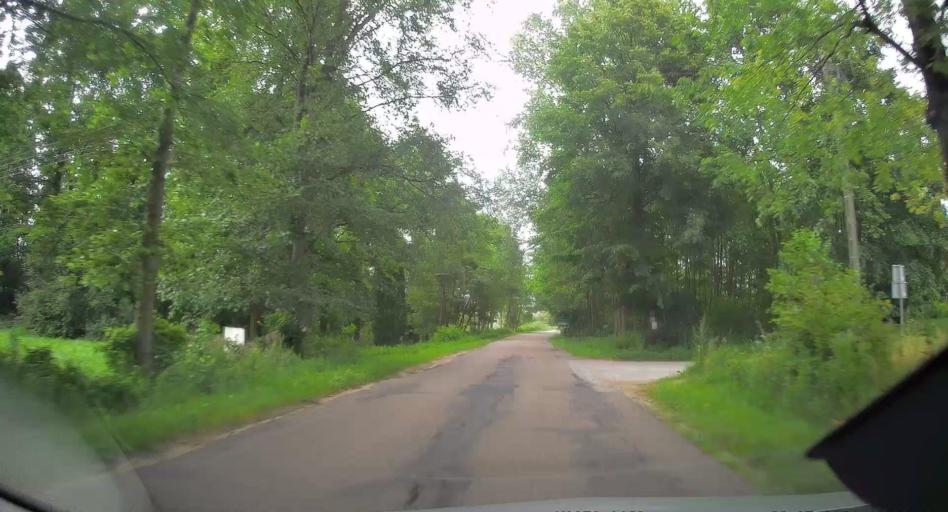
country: PL
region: Lodz Voivodeship
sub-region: Powiat rawski
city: Rawa Mazowiecka
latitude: 51.7458
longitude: 20.1858
